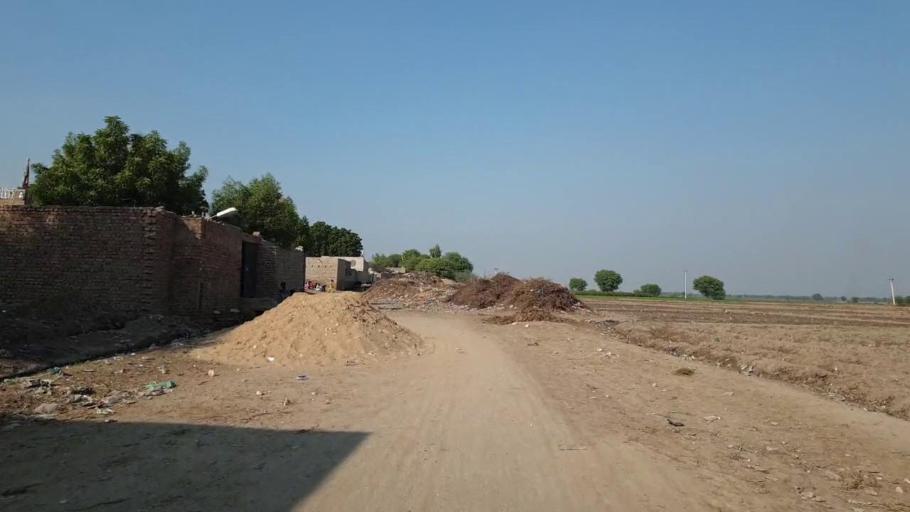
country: PK
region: Sindh
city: Sehwan
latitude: 26.4487
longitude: 67.8176
